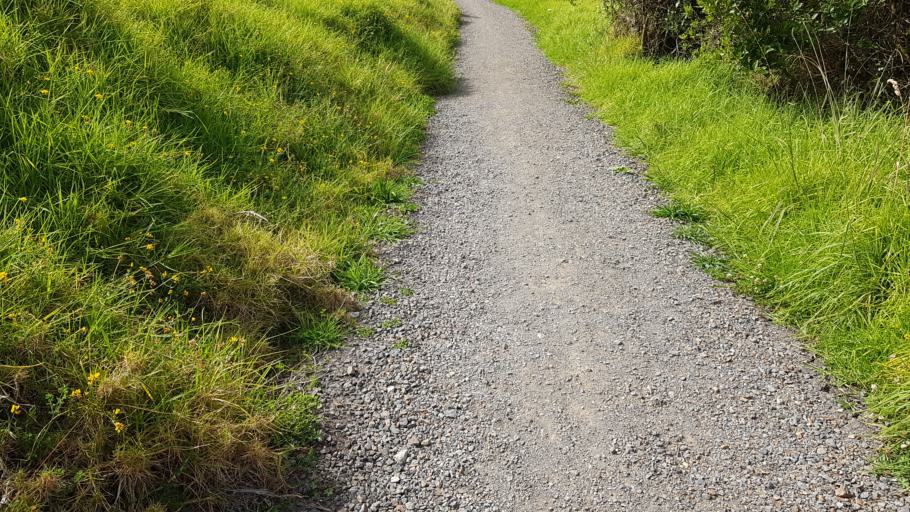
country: NZ
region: Auckland
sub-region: Auckland
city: Rothesay Bay
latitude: -36.6696
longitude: 174.7464
